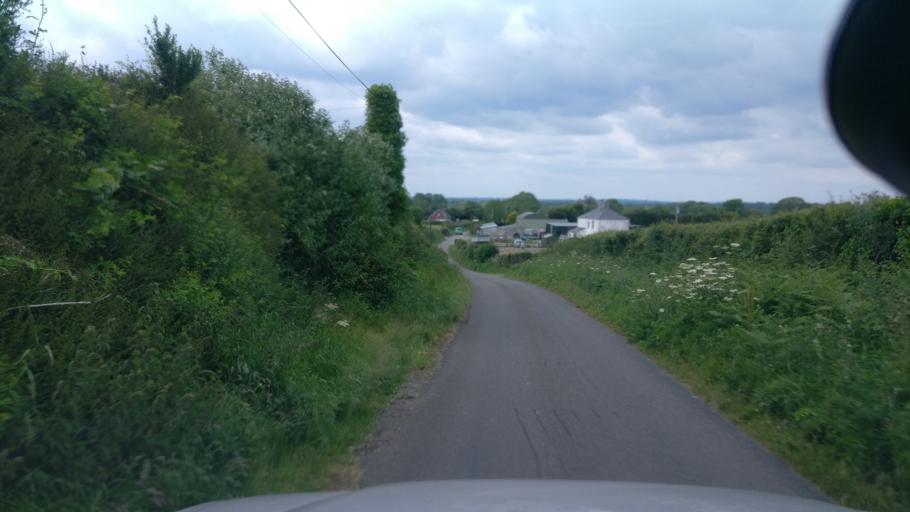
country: IE
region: Connaught
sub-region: County Galway
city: Ballinasloe
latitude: 53.2960
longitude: -8.3177
